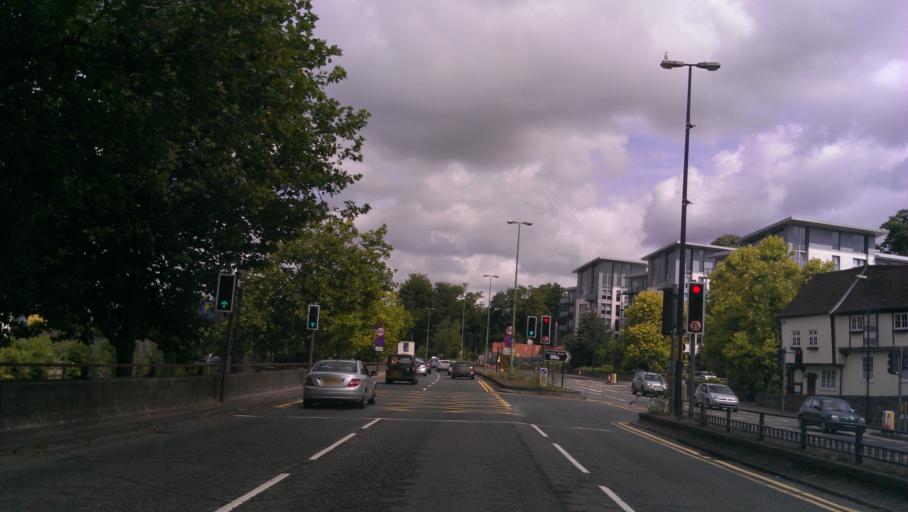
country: GB
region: England
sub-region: Kent
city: Maidstone
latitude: 51.2749
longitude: 0.5184
